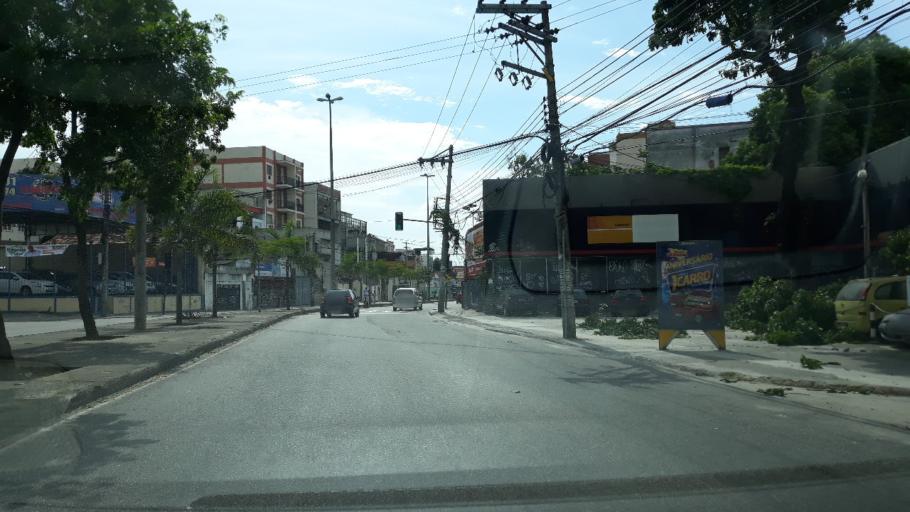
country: BR
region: Rio de Janeiro
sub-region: Sao Joao De Meriti
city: Sao Joao de Meriti
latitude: -22.8847
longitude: -43.3153
